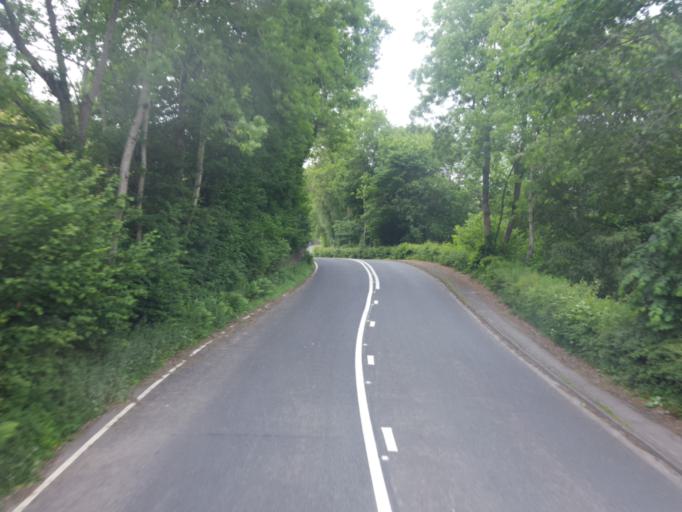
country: GB
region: England
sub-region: Cumbria
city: Keswick
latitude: 54.5872
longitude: -3.0960
